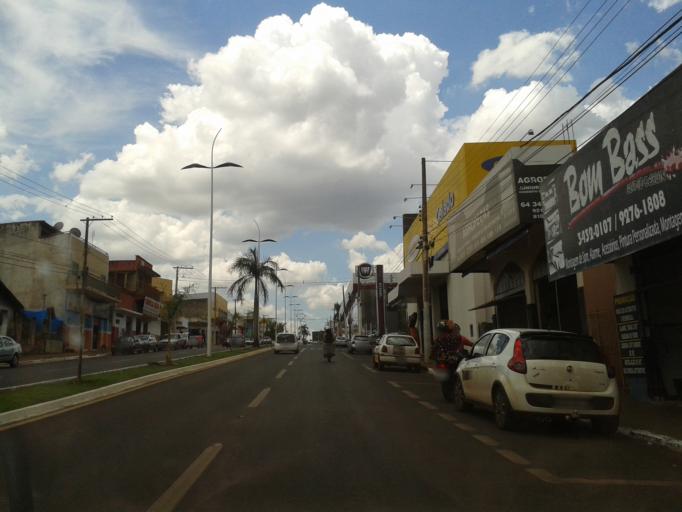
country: BR
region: Goias
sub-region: Itumbiara
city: Itumbiara
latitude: -18.4088
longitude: -49.2123
